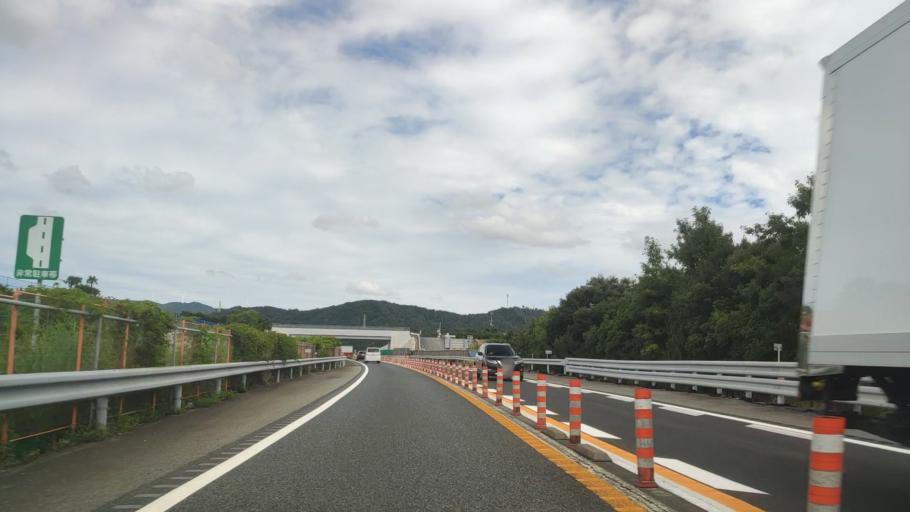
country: JP
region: Wakayama
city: Gobo
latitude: 33.9075
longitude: 135.1936
